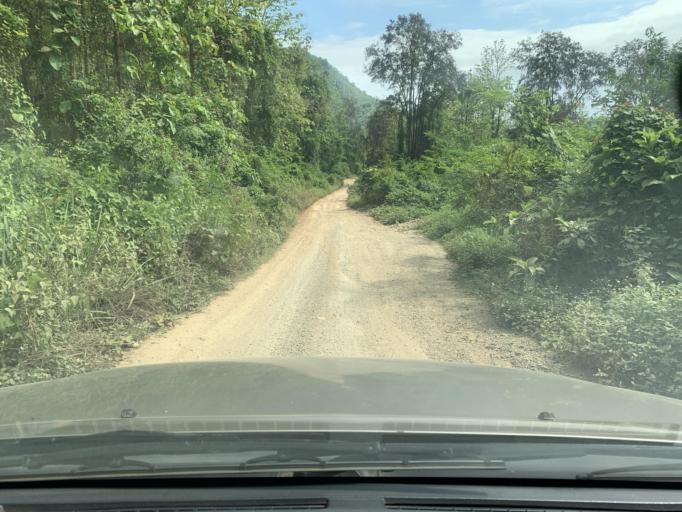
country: LA
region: Louangphabang
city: Louangphabang
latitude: 19.8878
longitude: 102.1975
